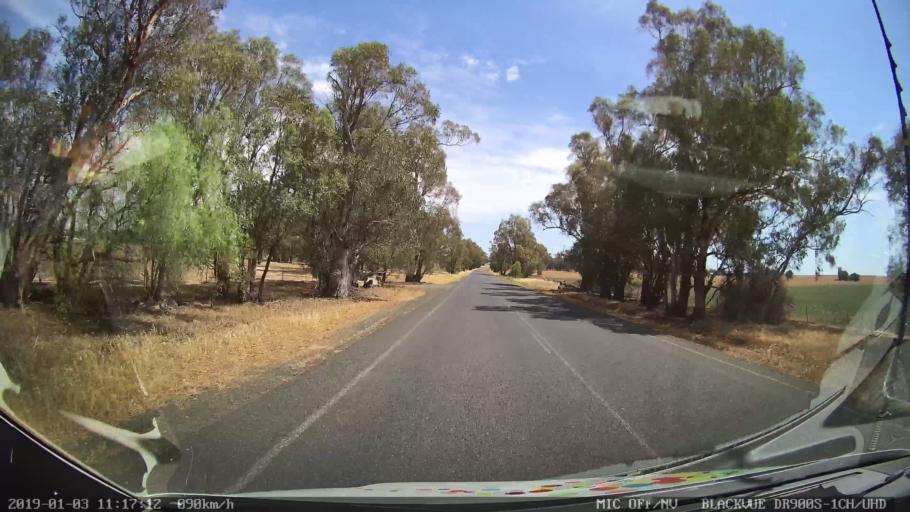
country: AU
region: New South Wales
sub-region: Young
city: Young
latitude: -34.1417
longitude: 148.2670
